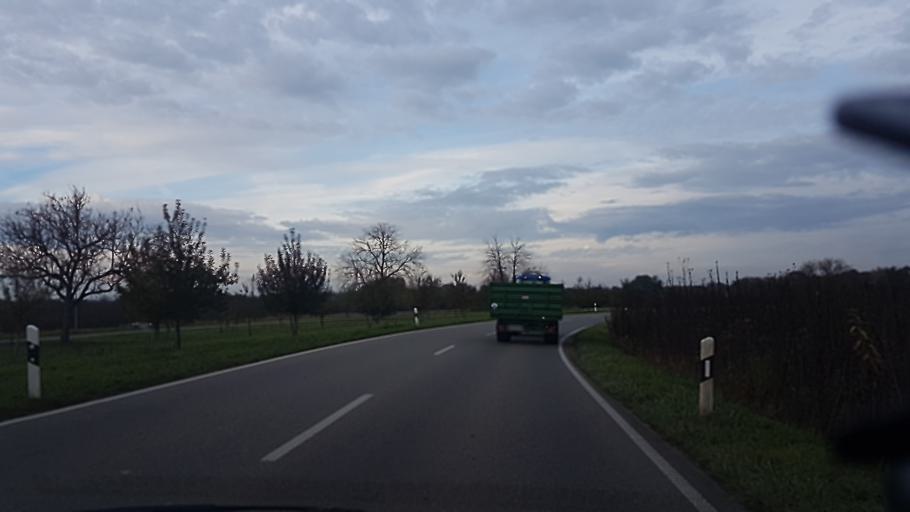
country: DE
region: Baden-Wuerttemberg
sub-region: Freiburg Region
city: Weisweil
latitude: 48.2078
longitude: 7.6836
